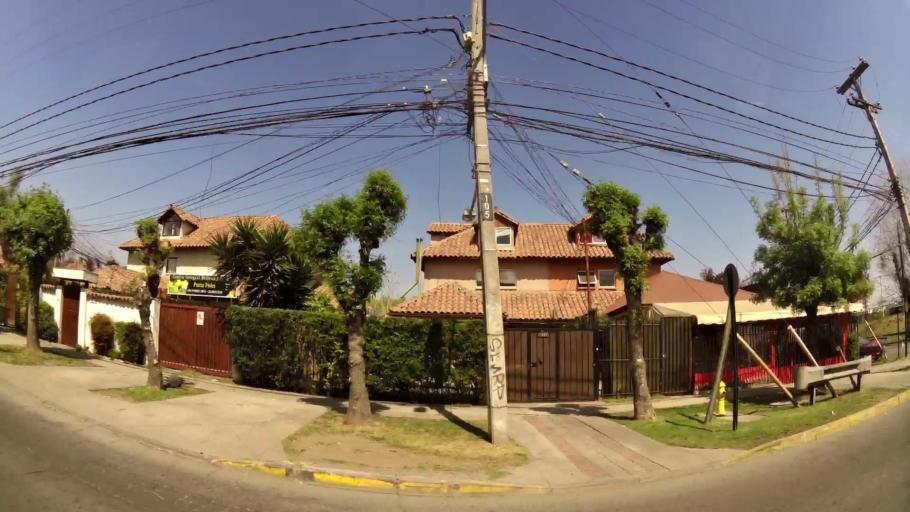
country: CL
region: Santiago Metropolitan
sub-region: Provincia de Santiago
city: Villa Presidente Frei, Nunoa, Santiago, Chile
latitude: -33.4739
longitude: -70.5542
